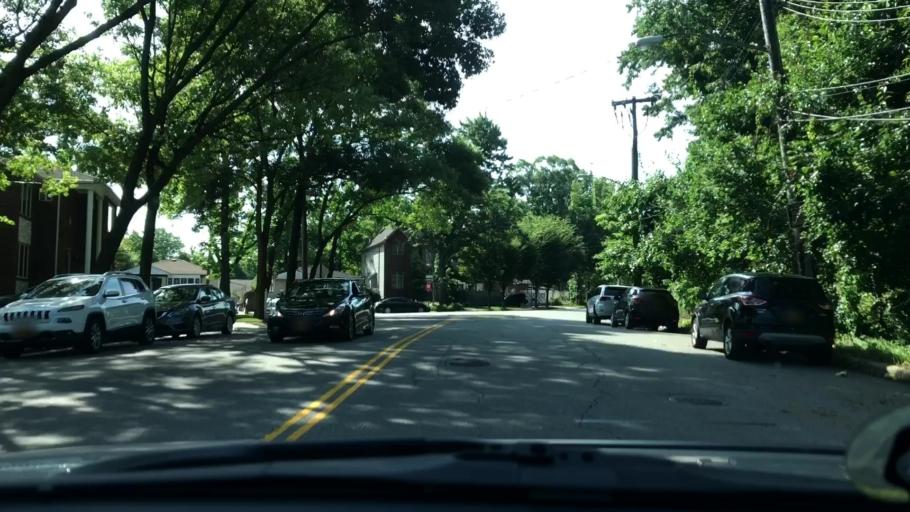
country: US
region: New York
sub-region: Richmond County
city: Staten Island
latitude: 40.5412
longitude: -74.1849
